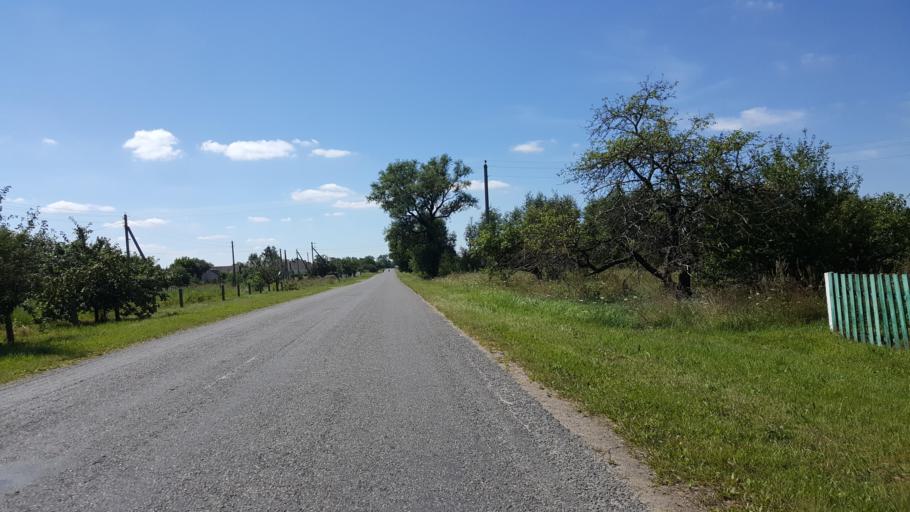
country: BY
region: Brest
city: Kamyanyets
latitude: 52.3726
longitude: 23.6293
